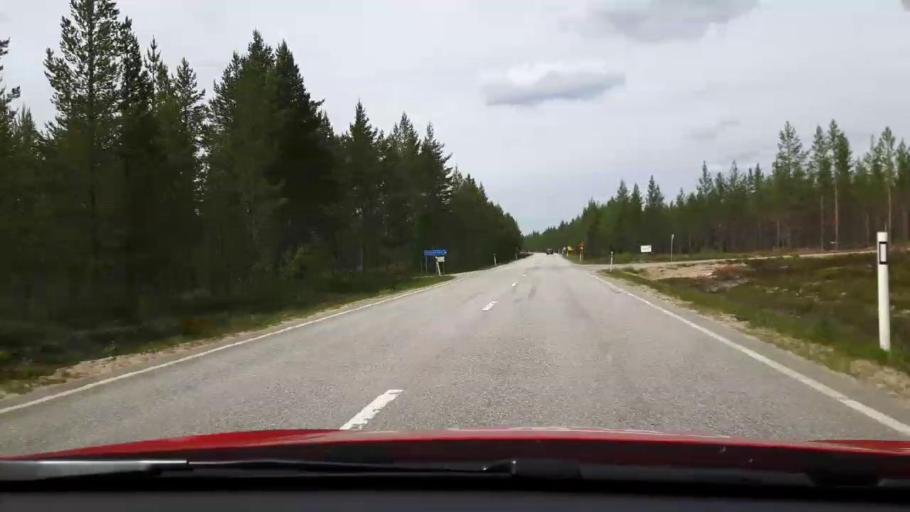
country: SE
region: Jaemtland
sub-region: Harjedalens Kommun
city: Sveg
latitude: 62.0557
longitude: 14.3012
